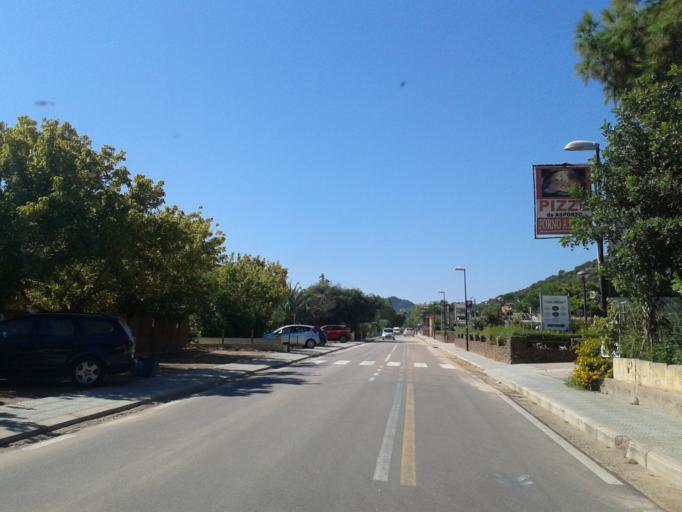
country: IT
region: Sardinia
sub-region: Provincia di Cagliari
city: Olia Speciosa
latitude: 39.2515
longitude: 9.5728
